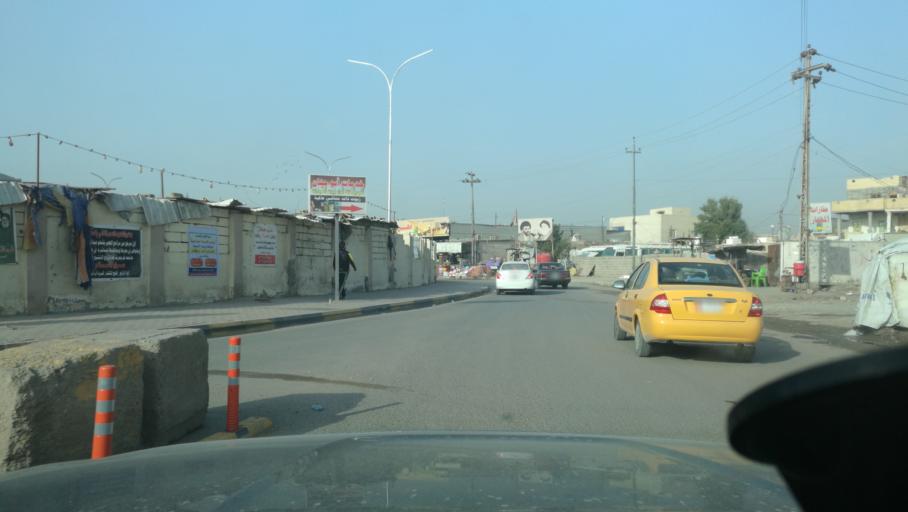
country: IQ
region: Basra Governorate
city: Al Basrah al Qadimah
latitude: 30.4944
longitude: 47.8194
